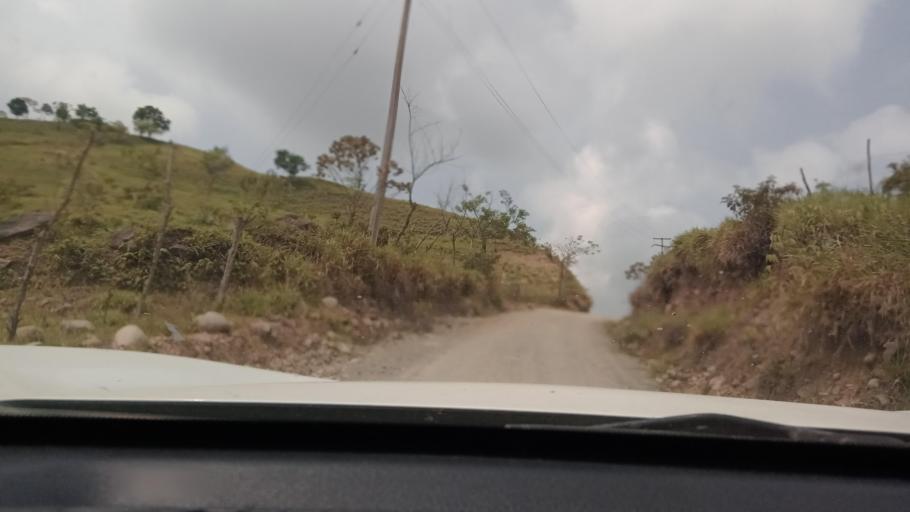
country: MX
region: Tabasco
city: Chontalpa
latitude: 17.4924
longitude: -93.6643
